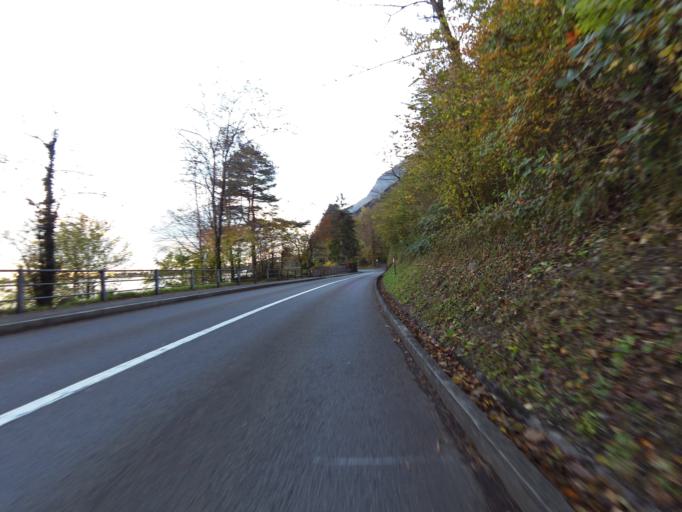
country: CH
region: Uri
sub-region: Uri
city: Flueelen
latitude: 46.8937
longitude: 8.5953
